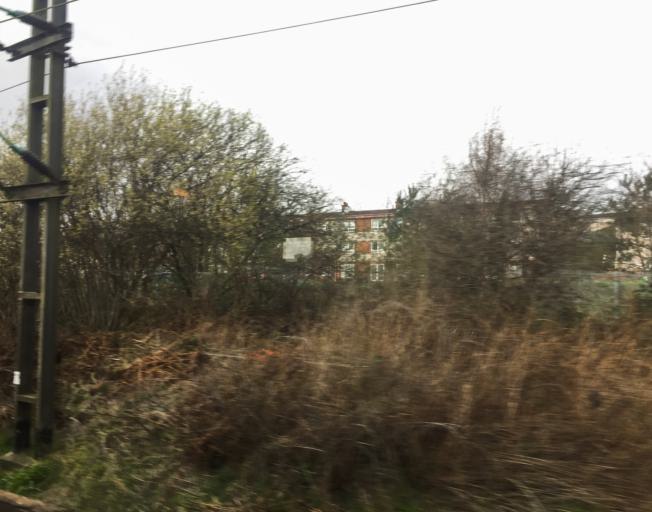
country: GB
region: Scotland
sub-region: West Dunbartonshire
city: Clydebank
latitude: 55.9043
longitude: -4.3885
